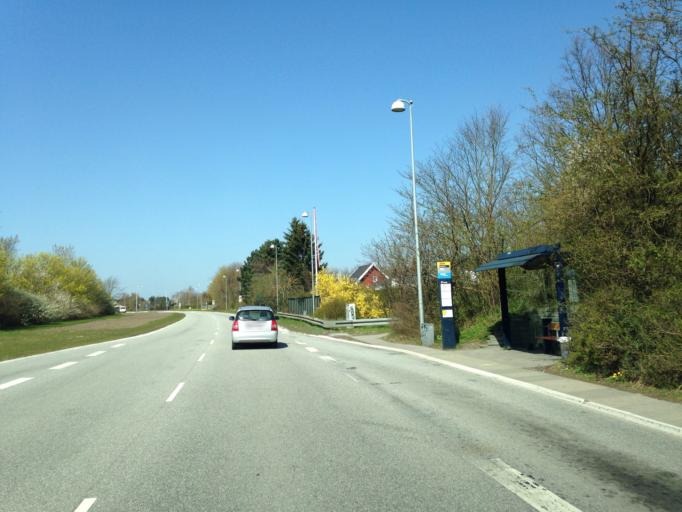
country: DK
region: Zealand
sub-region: Greve Kommune
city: Greve
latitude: 55.5885
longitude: 12.2879
